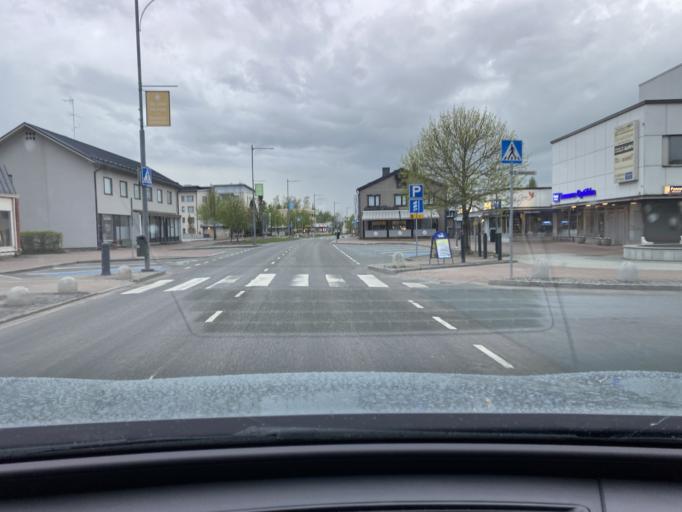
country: FI
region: Varsinais-Suomi
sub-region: Salo
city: Somero
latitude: 60.6301
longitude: 23.5135
